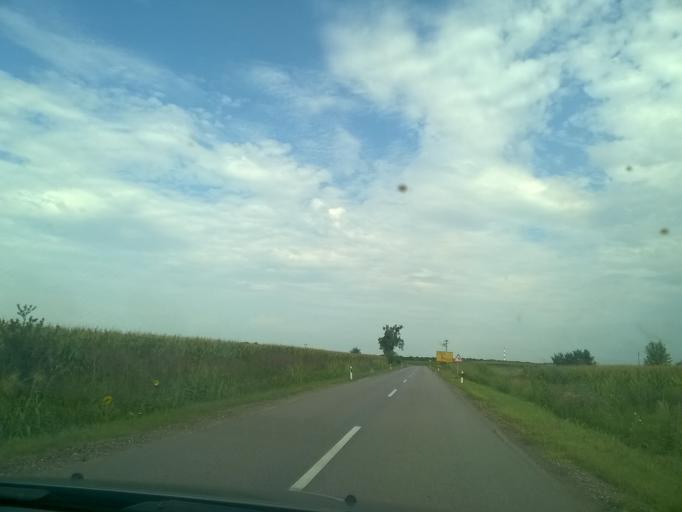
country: RS
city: Ecka
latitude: 45.3204
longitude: 20.4602
